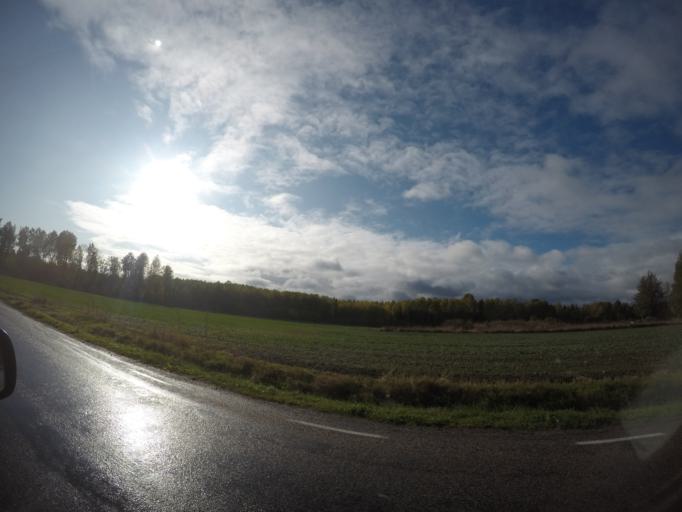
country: SE
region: Soedermanland
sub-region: Eskilstuna Kommun
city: Kvicksund
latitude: 59.3352
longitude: 16.2522
